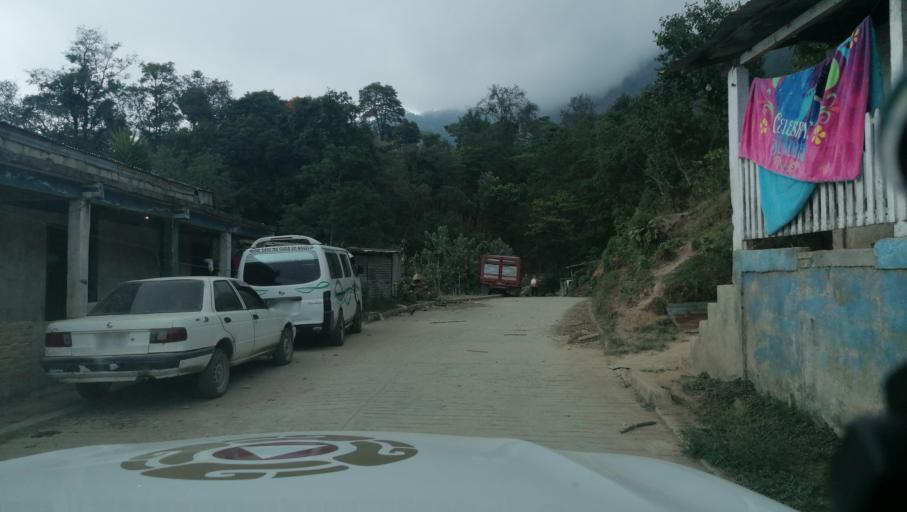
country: GT
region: San Marcos
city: Tacana
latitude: 15.2001
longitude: -92.1788
